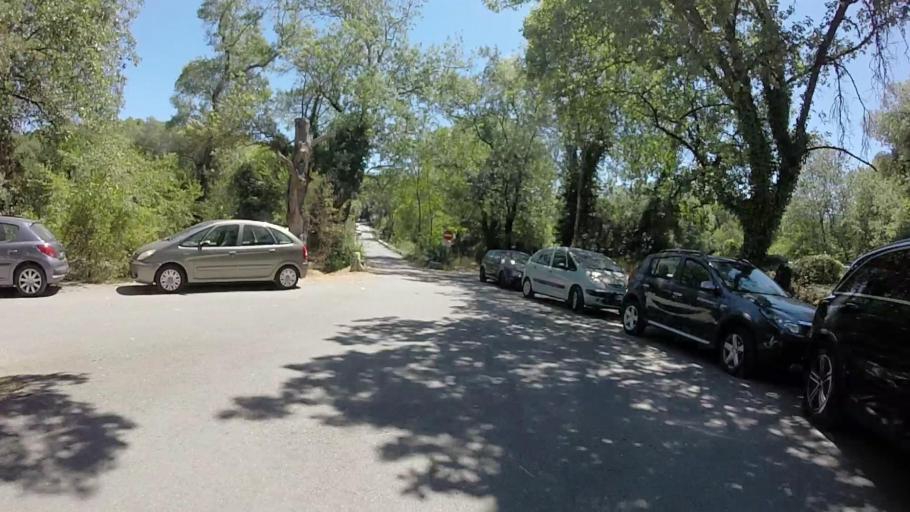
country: FR
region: Provence-Alpes-Cote d'Azur
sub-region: Departement des Alpes-Maritimes
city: Vallauris
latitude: 43.6158
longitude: 7.0413
